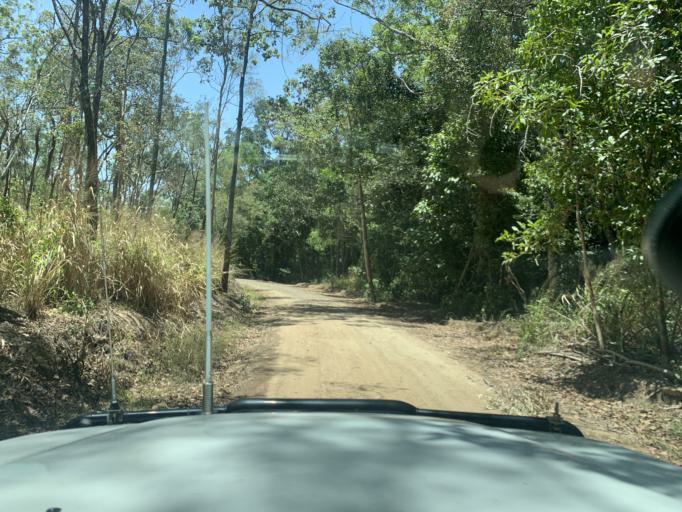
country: AU
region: Queensland
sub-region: Cairns
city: Redlynch
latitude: -16.9330
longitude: 145.6019
